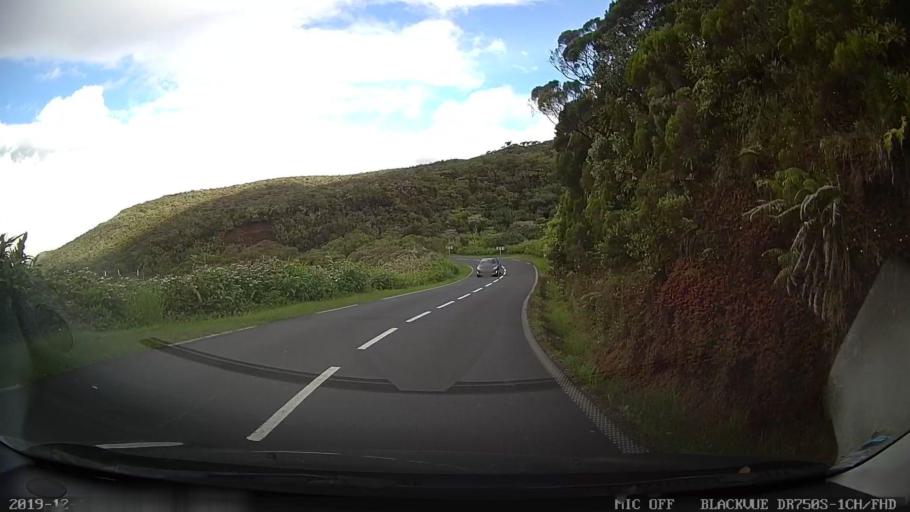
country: RE
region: Reunion
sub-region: Reunion
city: Cilaos
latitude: -21.1632
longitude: 55.5913
